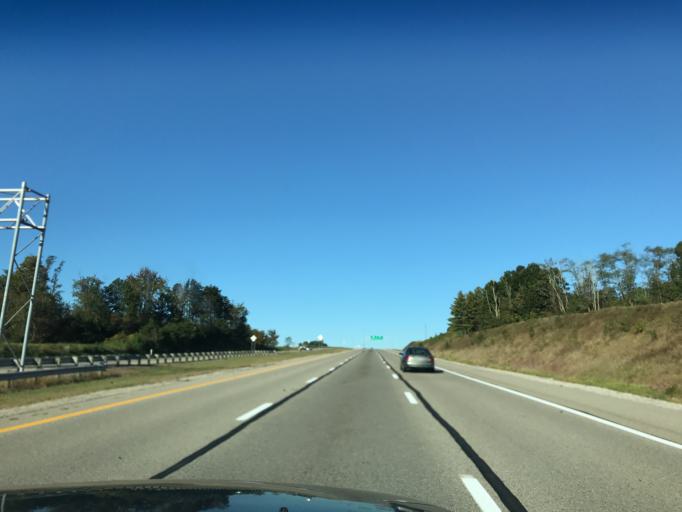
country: US
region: West Virginia
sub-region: Wood County
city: Blennerhassett
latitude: 39.2571
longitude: -81.6344
